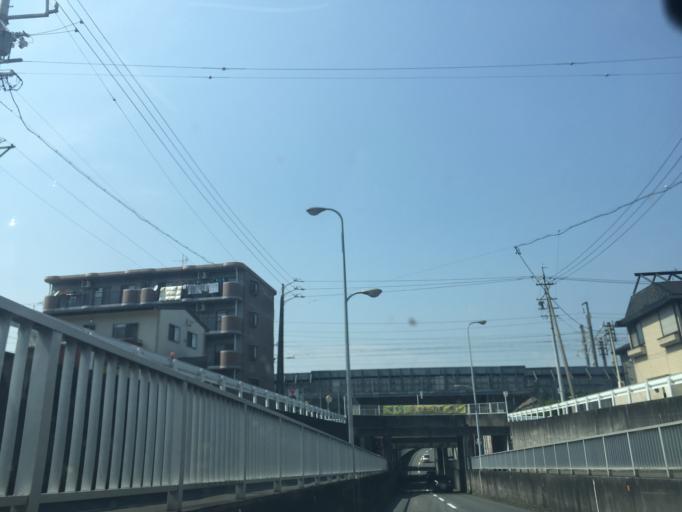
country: JP
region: Shizuoka
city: Kakegawa
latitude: 34.7676
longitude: 138.0082
